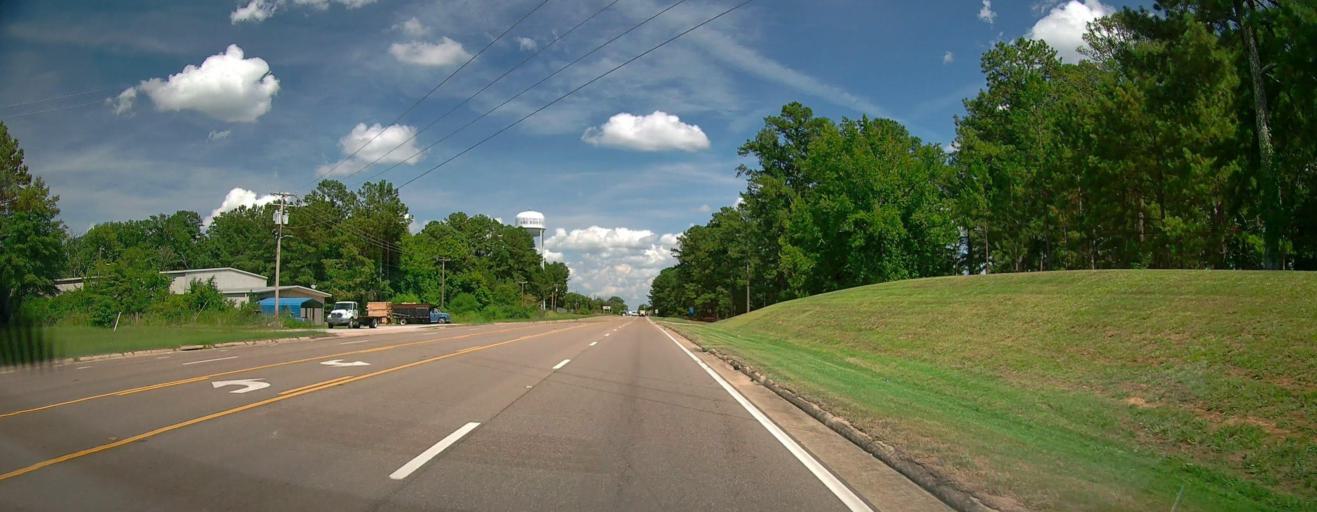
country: US
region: Mississippi
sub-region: Monroe County
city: Aberdeen
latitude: 33.8148
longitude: -88.5614
